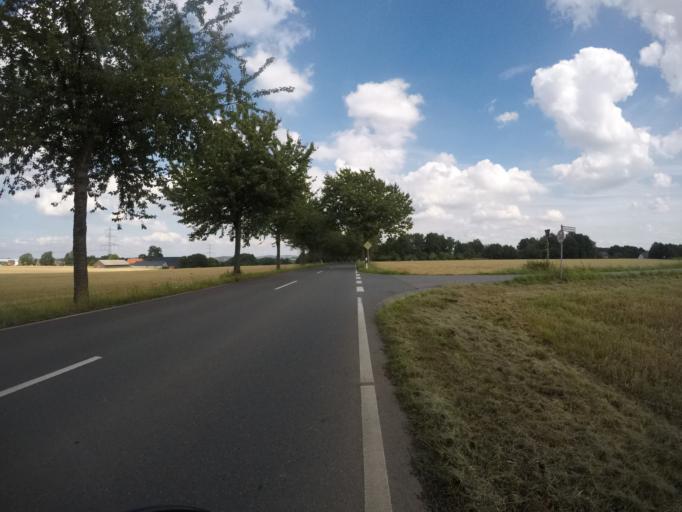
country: DE
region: North Rhine-Westphalia
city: Enger
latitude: 52.1121
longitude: 8.5799
